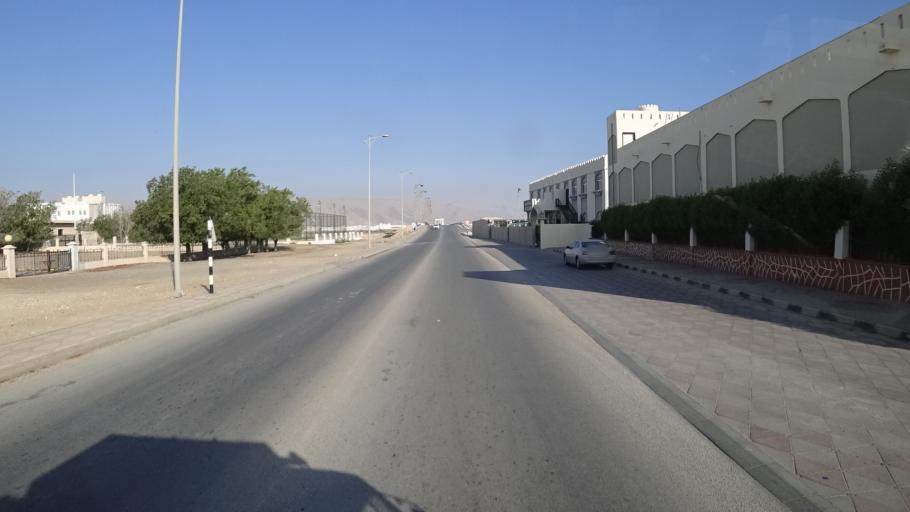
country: OM
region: Ash Sharqiyah
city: Sur
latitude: 22.5955
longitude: 59.4931
